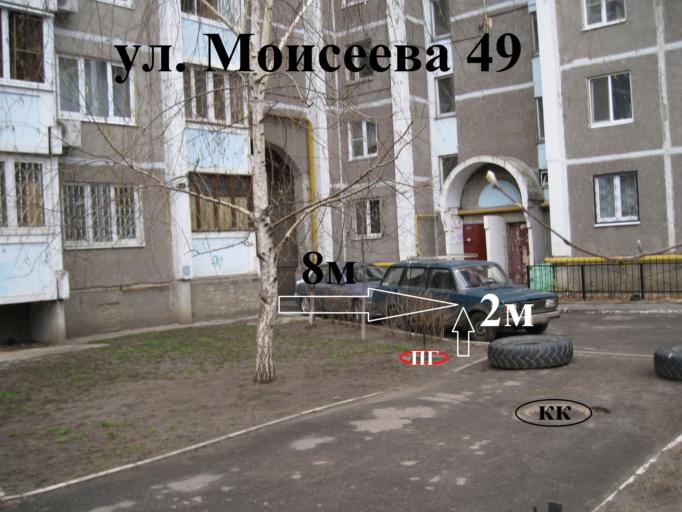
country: RU
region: Voronezj
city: Voronezh
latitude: 51.6497
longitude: 39.1796
